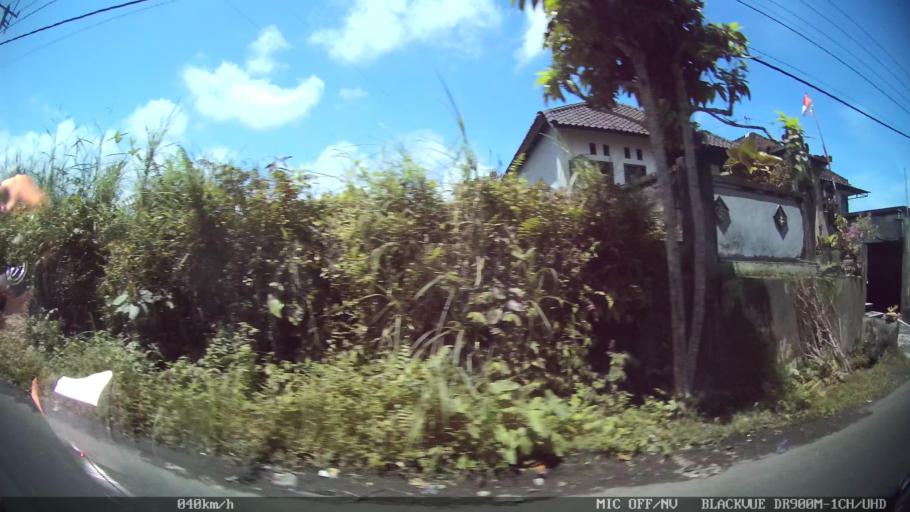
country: ID
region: Bali
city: Banjar Kelodan
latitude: -8.5277
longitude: 115.3356
